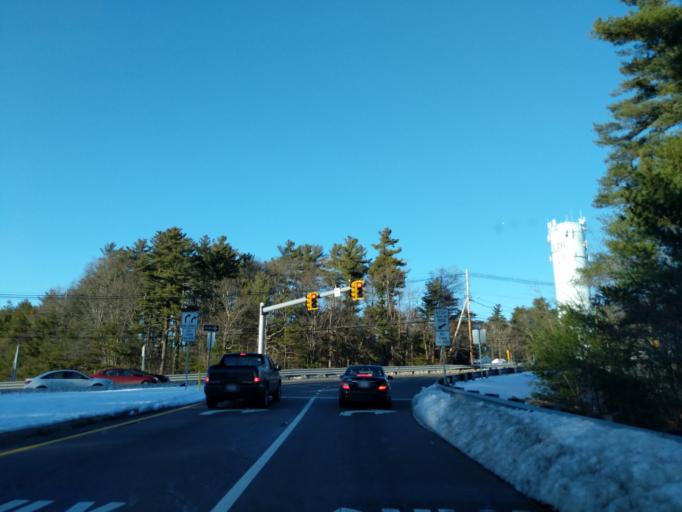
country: US
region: Massachusetts
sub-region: Bristol County
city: Raynham Center
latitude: 41.9058
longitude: -71.0405
